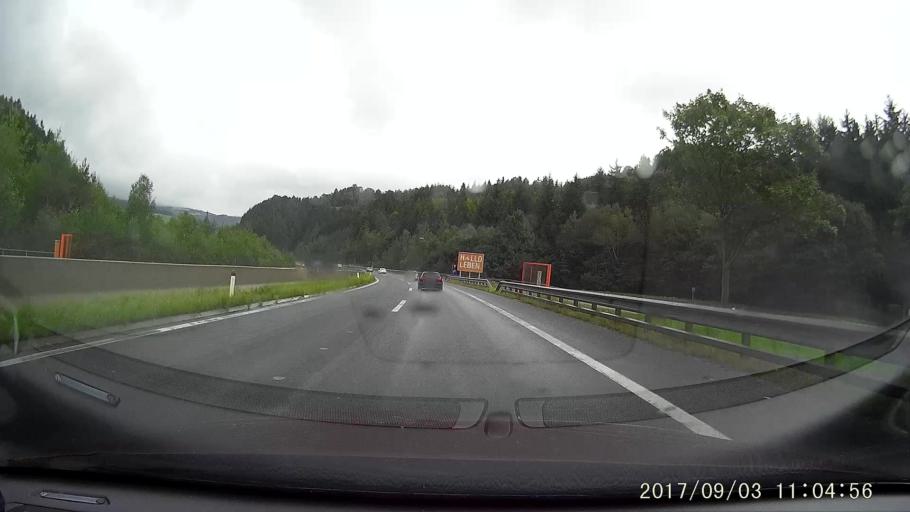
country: AT
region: Lower Austria
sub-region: Politischer Bezirk Neunkirchen
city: Edlitz
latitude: 47.5767
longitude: 16.1130
